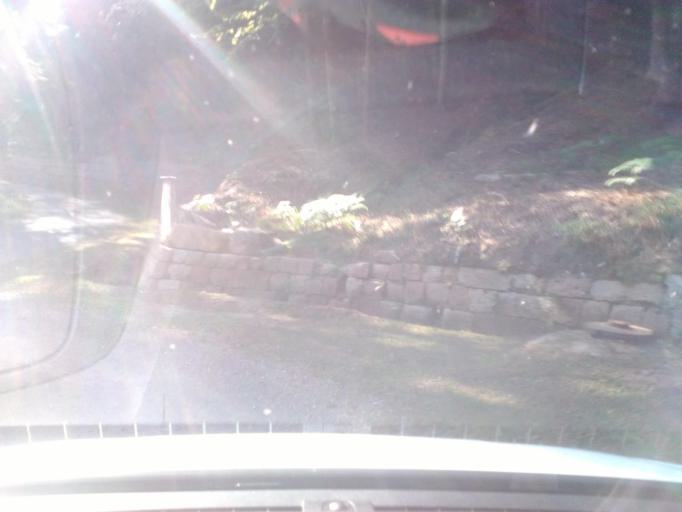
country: FR
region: Lorraine
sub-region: Departement des Vosges
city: Senones
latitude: 48.4156
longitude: 6.9741
